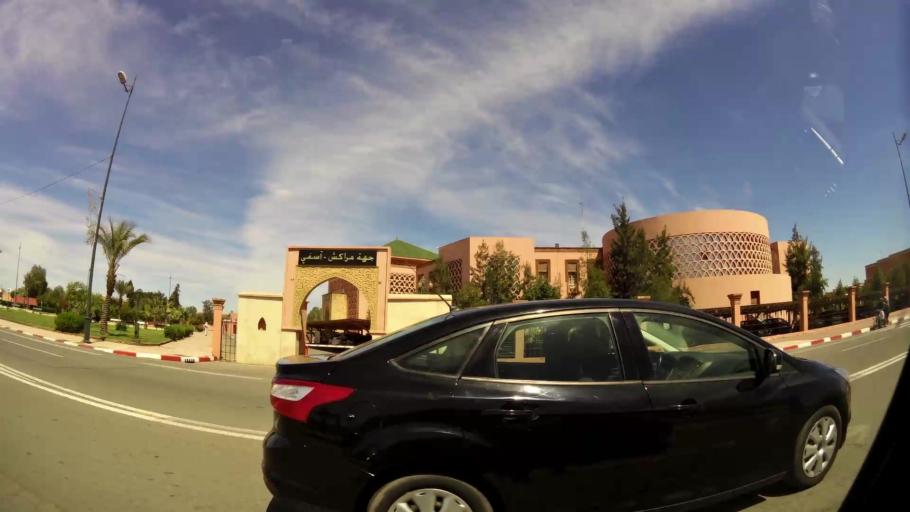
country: MA
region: Marrakech-Tensift-Al Haouz
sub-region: Marrakech
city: Marrakesh
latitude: 31.6134
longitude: -7.9750
